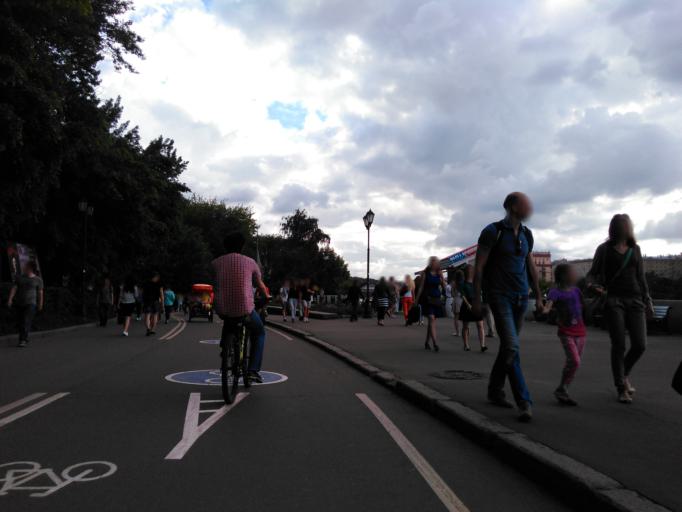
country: RU
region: Moscow
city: Novyye Cheremushki
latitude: 55.7218
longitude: 37.5902
